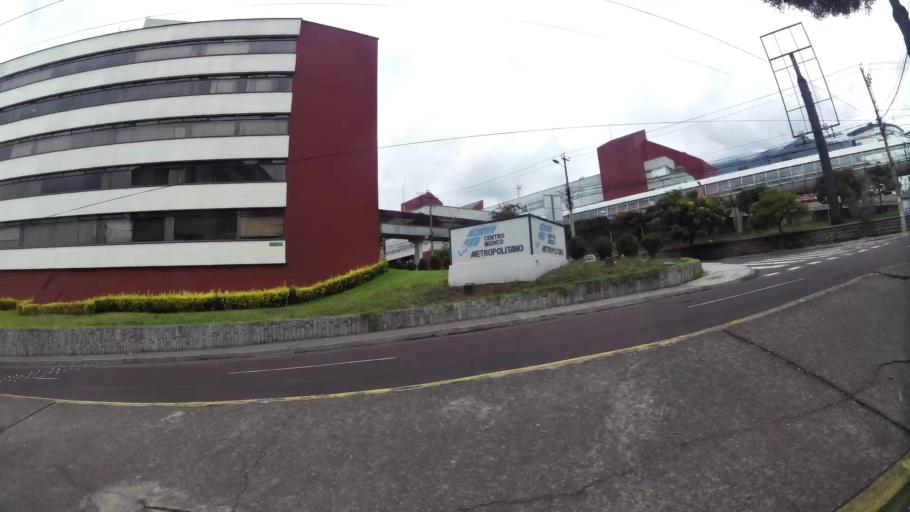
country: EC
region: Pichincha
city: Quito
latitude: -0.1837
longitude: -78.5031
